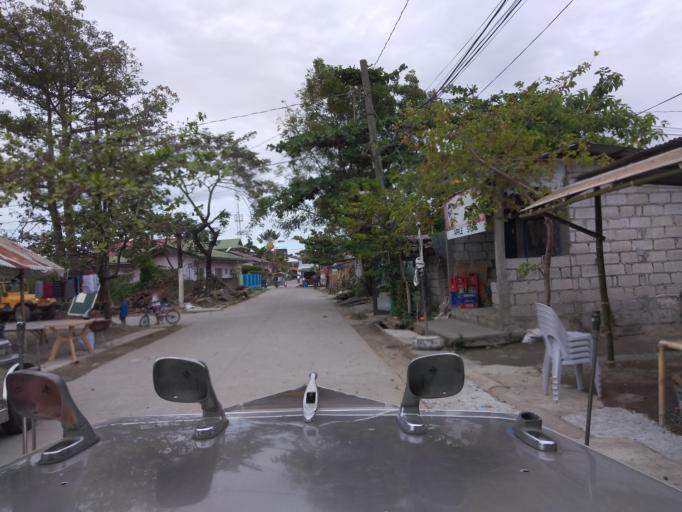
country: PH
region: Central Luzon
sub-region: Province of Pampanga
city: Mexico
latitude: 15.0619
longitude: 120.7267
